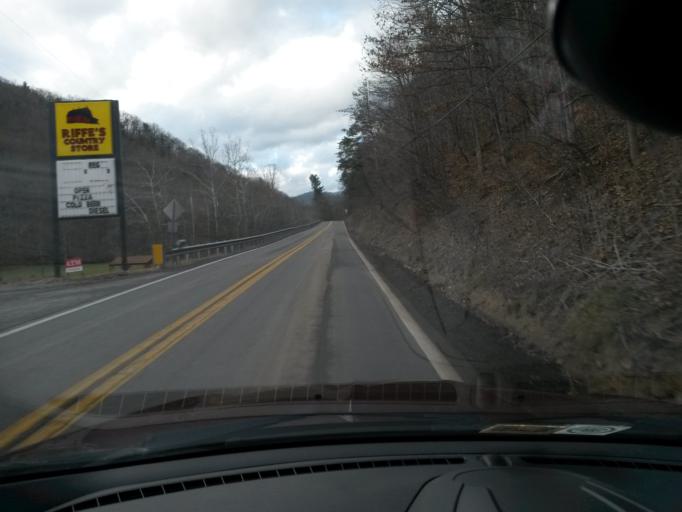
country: US
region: West Virginia
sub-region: Monroe County
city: Union
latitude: 37.5117
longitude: -80.6122
